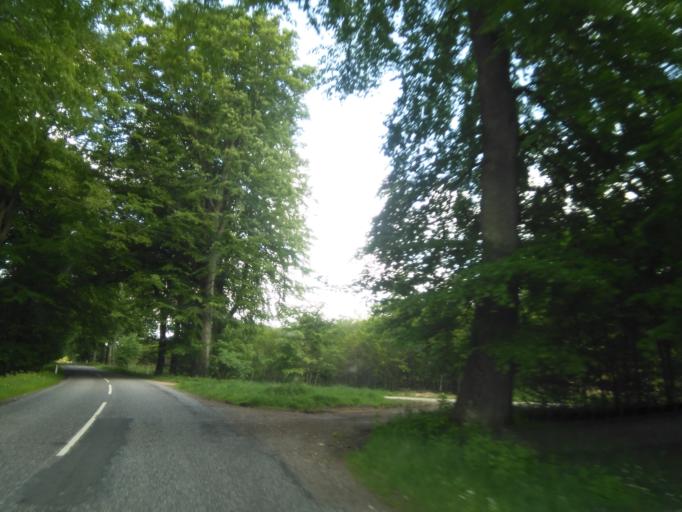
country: DK
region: Central Jutland
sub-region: Favrskov Kommune
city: Hammel
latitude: 56.2395
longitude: 9.9335
